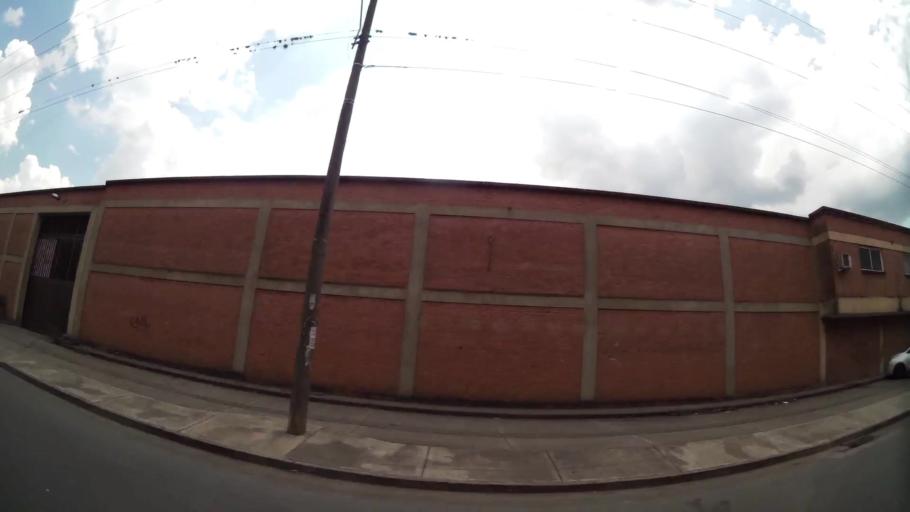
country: CO
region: Valle del Cauca
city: Cali
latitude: 3.4723
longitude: -76.5065
